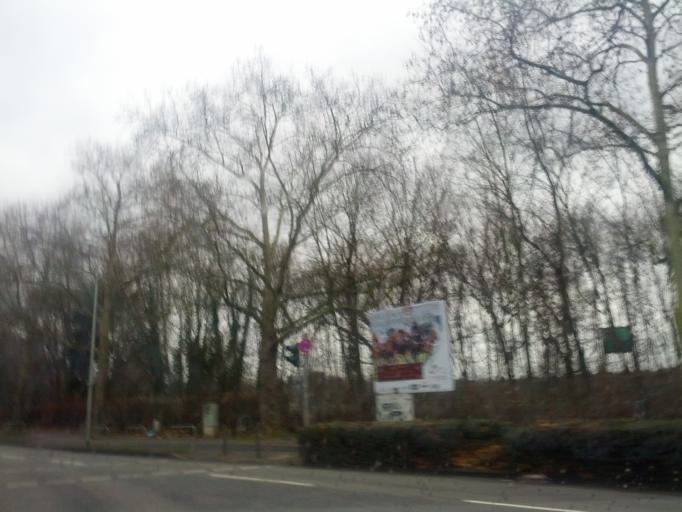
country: DE
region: Hesse
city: Niederrad
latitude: 50.0860
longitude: 8.6499
